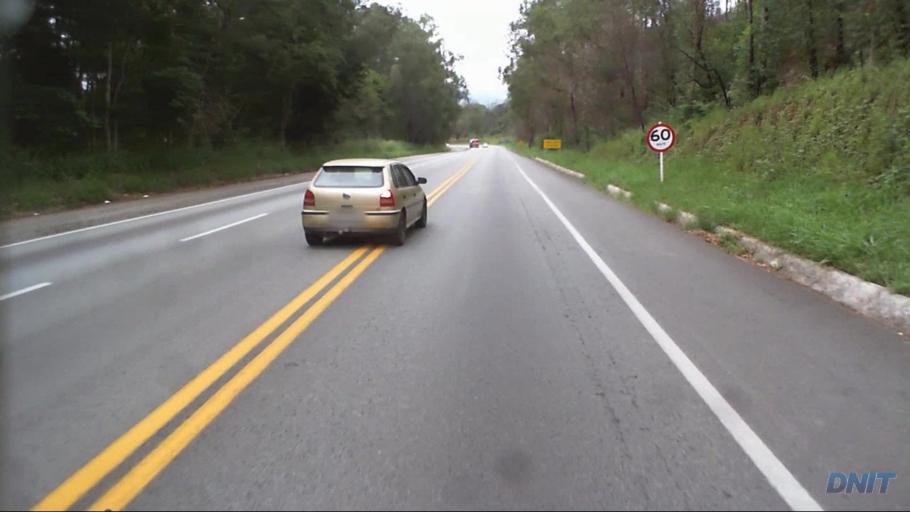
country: BR
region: Minas Gerais
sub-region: Joao Monlevade
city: Joao Monlevade
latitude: -19.8504
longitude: -43.1101
